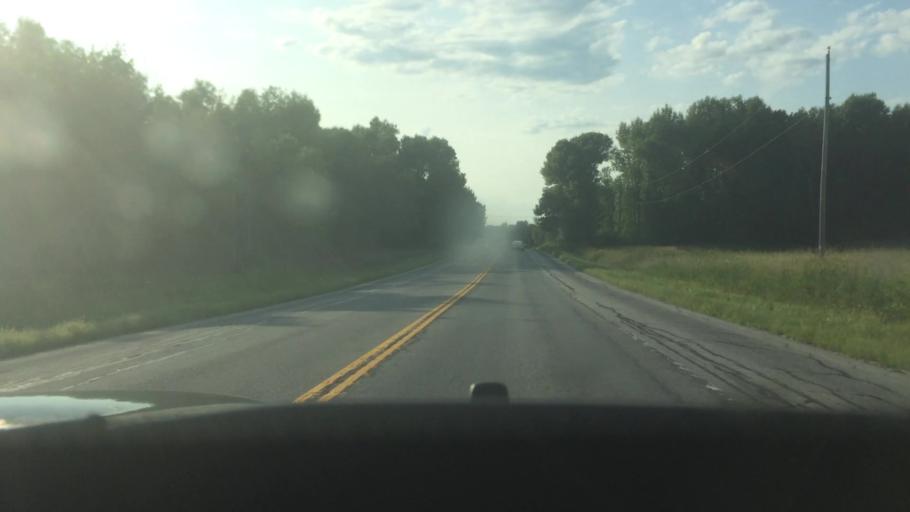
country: US
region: New York
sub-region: St. Lawrence County
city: Canton
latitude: 44.6047
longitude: -75.2041
